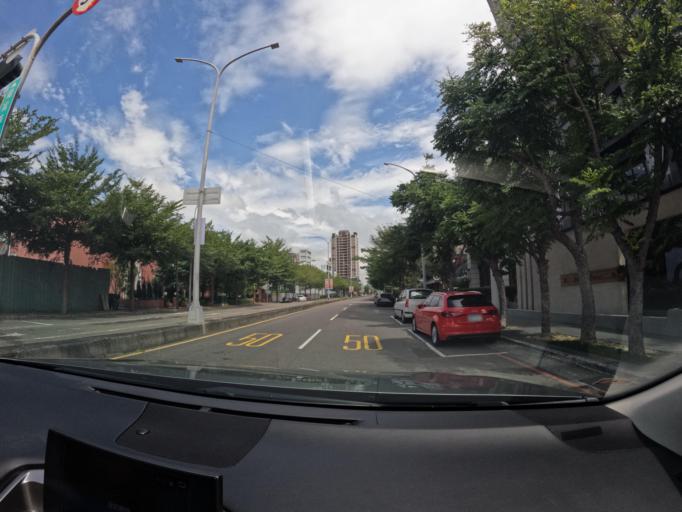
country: TW
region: Taiwan
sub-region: Taichung City
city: Taichung
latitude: 24.1383
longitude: 120.6259
